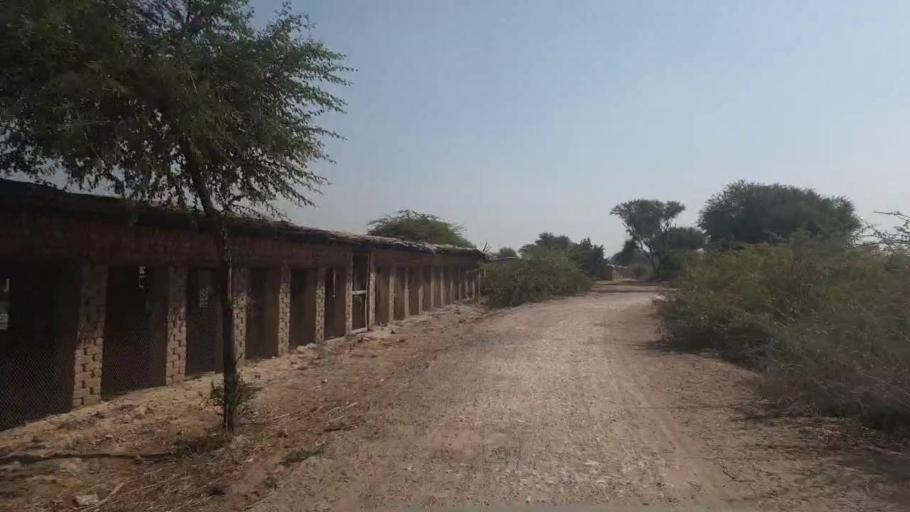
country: PK
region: Sindh
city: Chambar
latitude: 25.2301
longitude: 68.8213
